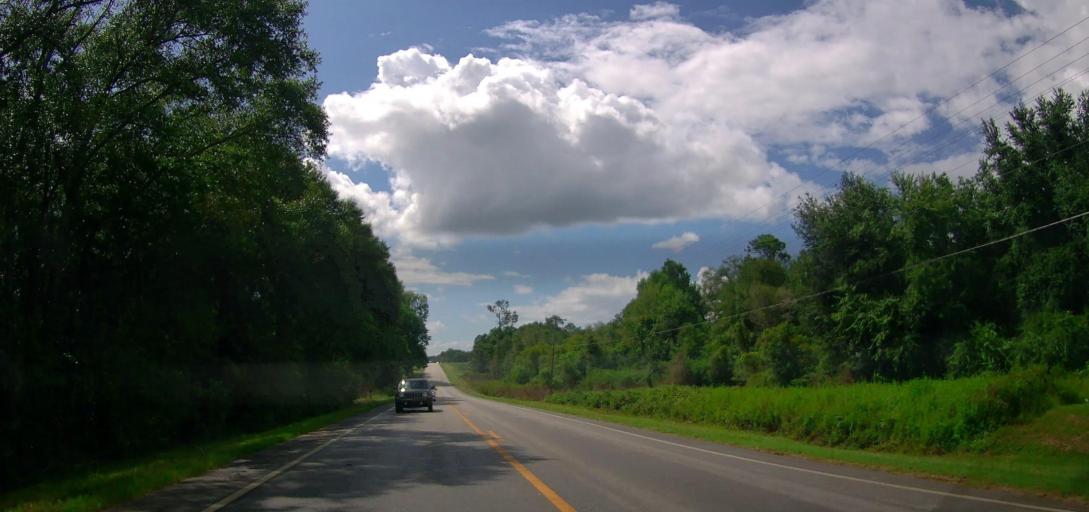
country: US
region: Georgia
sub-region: Coffee County
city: Broxton
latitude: 31.5517
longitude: -82.9559
